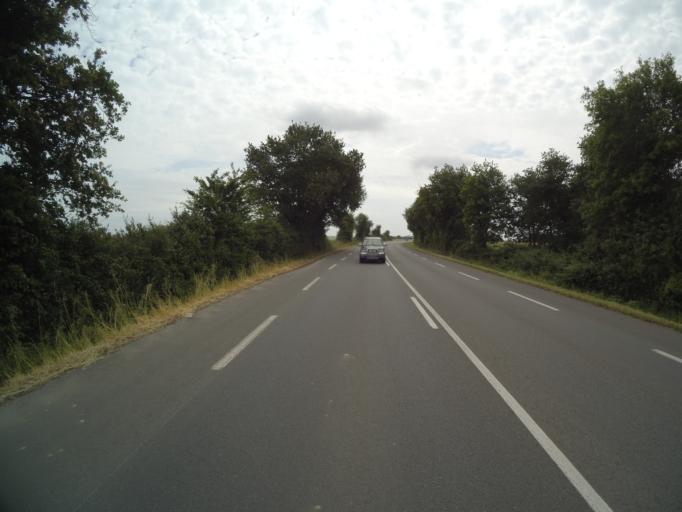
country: FR
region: Pays de la Loire
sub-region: Departement de la Vendee
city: Chavagnes-en-Paillers
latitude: 46.9210
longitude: -1.2481
